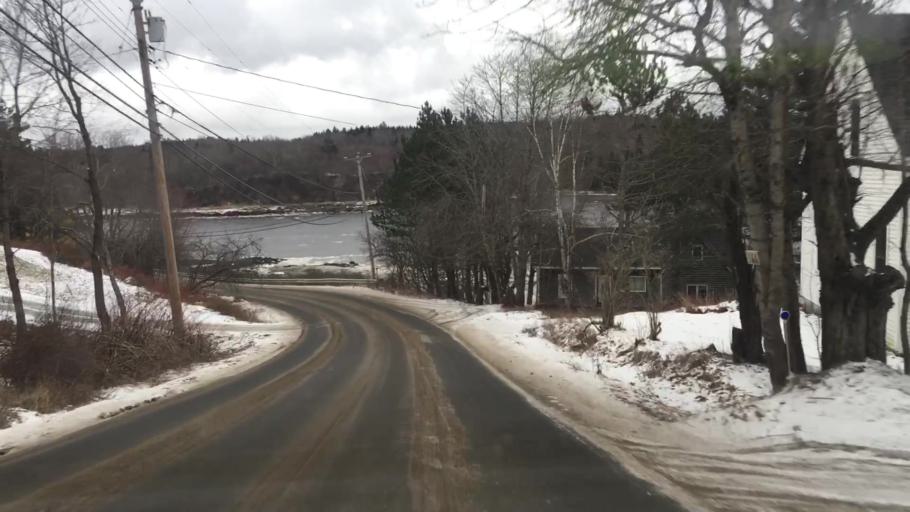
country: US
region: Maine
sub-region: Washington County
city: Machiasport
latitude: 44.6958
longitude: -67.3953
